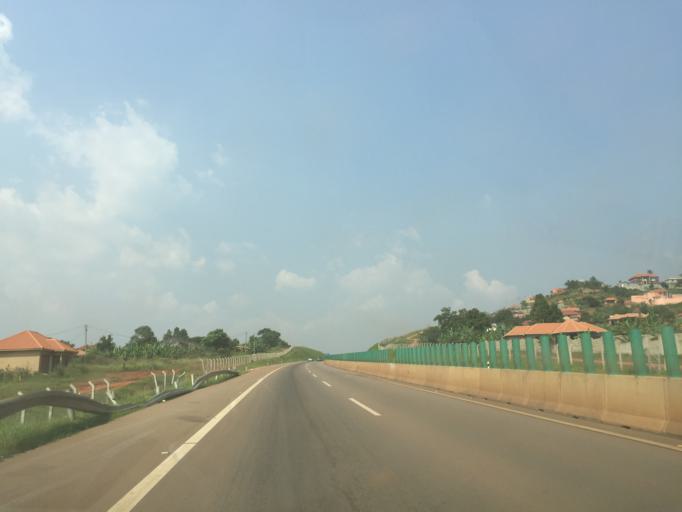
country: UG
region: Central Region
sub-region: Wakiso District
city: Kajansi
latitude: 0.1702
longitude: 32.5148
